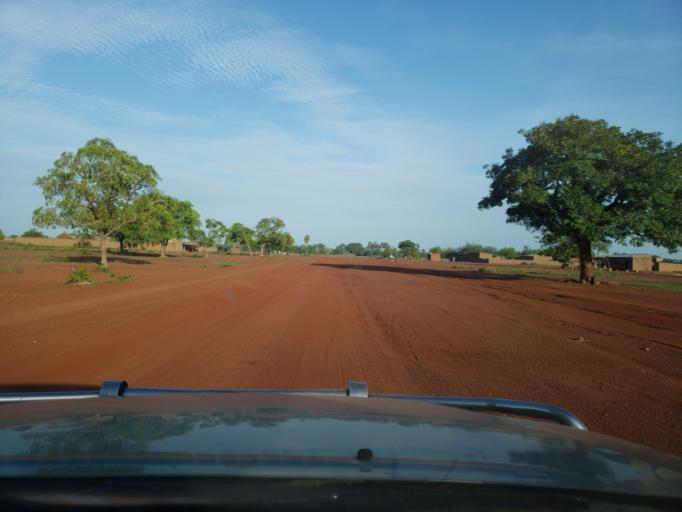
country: ML
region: Sikasso
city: Koutiala
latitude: 12.4047
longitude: -5.5338
